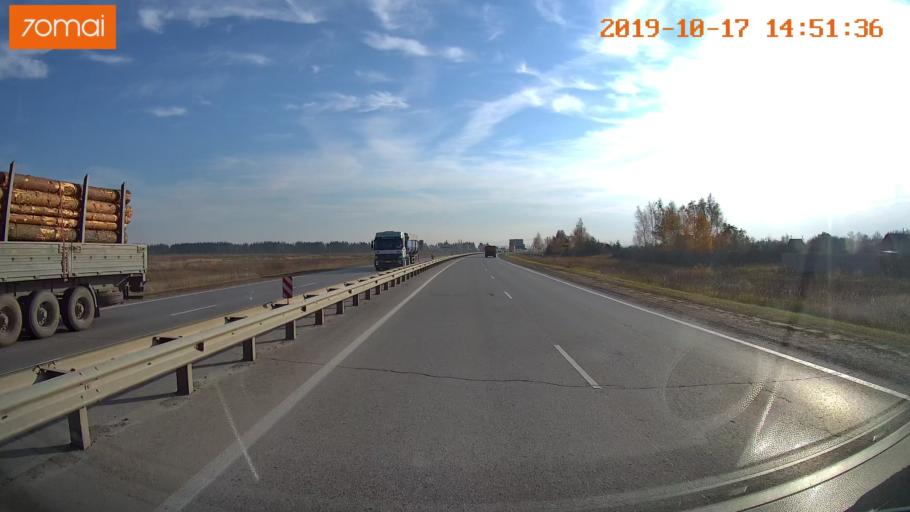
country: RU
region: Rjazan
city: Polyany
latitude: 54.7173
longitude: 39.8488
